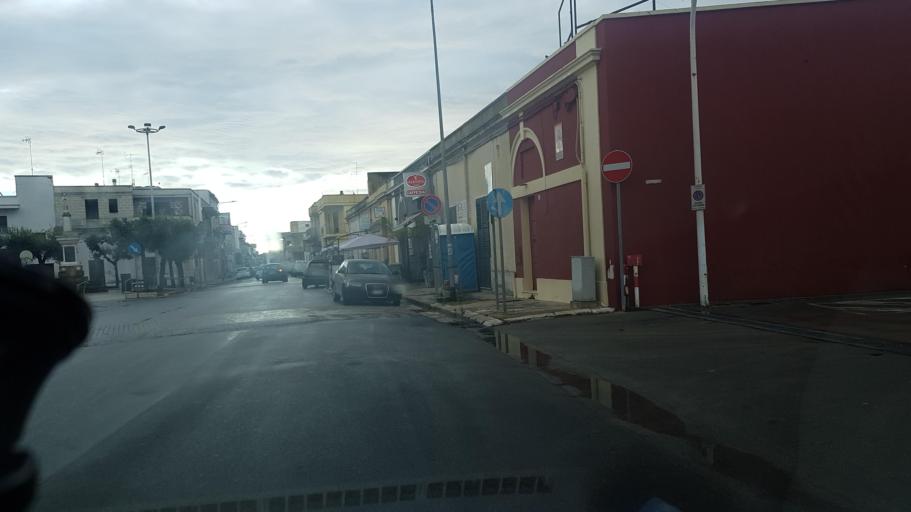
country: IT
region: Apulia
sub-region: Provincia di Lecce
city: Carmiano
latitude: 40.3448
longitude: 18.0454
